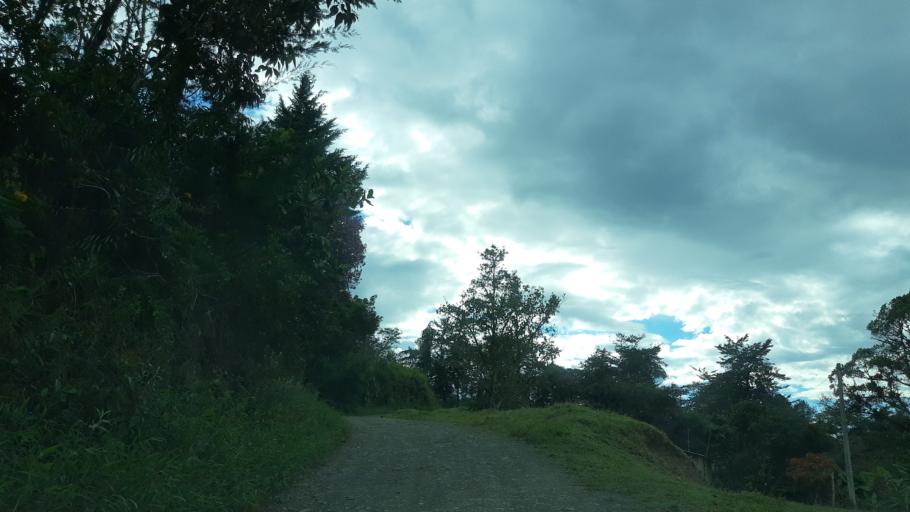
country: CO
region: Boyaca
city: Garagoa
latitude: 5.0159
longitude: -73.3349
